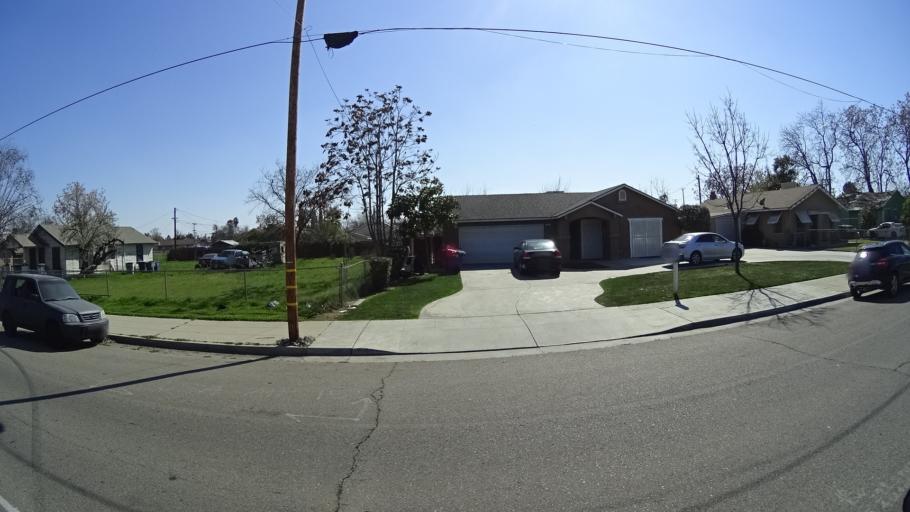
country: US
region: California
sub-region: Fresno County
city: Fresno
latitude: 36.7359
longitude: -119.8143
